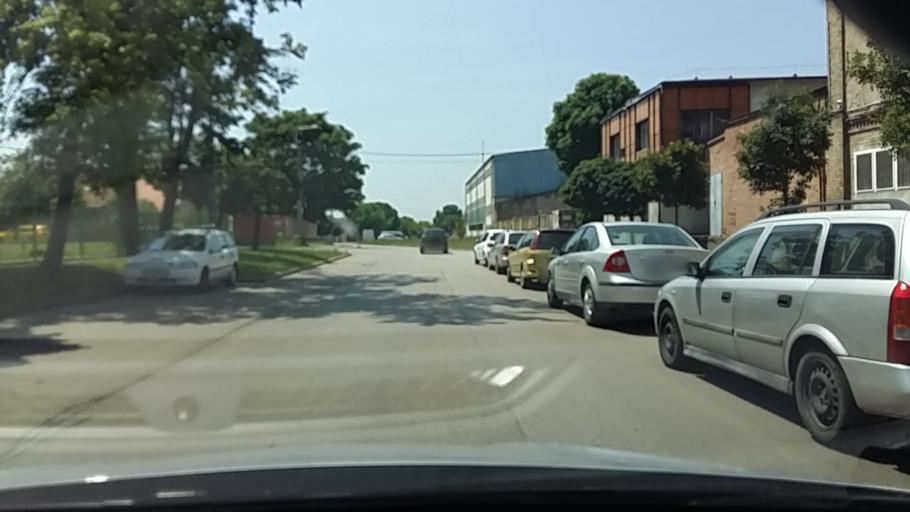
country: HU
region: Budapest
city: Budapest X. keruelet
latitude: 47.4765
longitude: 19.1372
